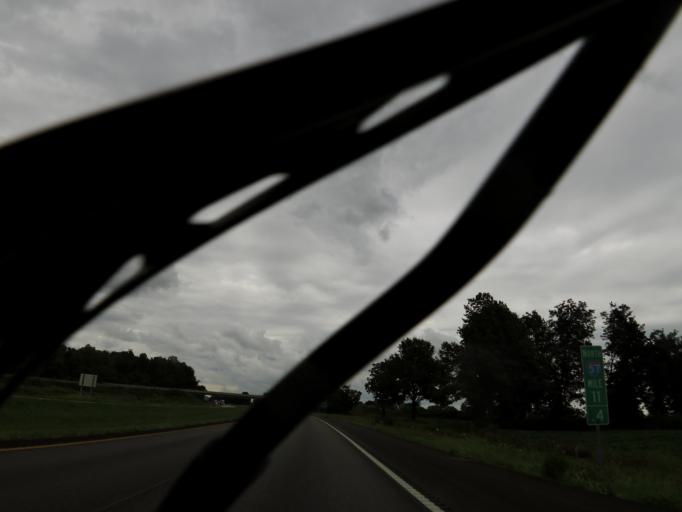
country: US
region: Missouri
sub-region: Mississippi County
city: Charleston
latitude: 36.9071
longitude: -89.3363
